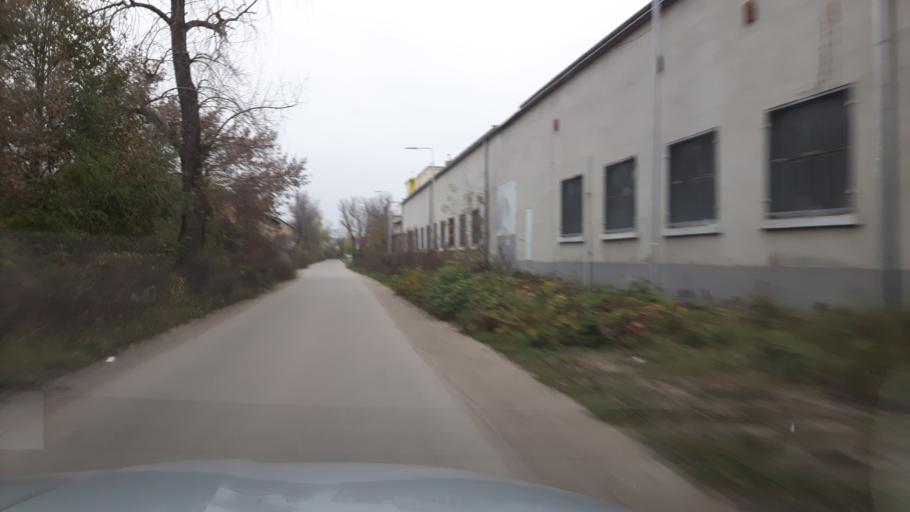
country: PL
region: Masovian Voivodeship
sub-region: Warszawa
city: Targowek
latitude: 52.2800
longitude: 21.0232
